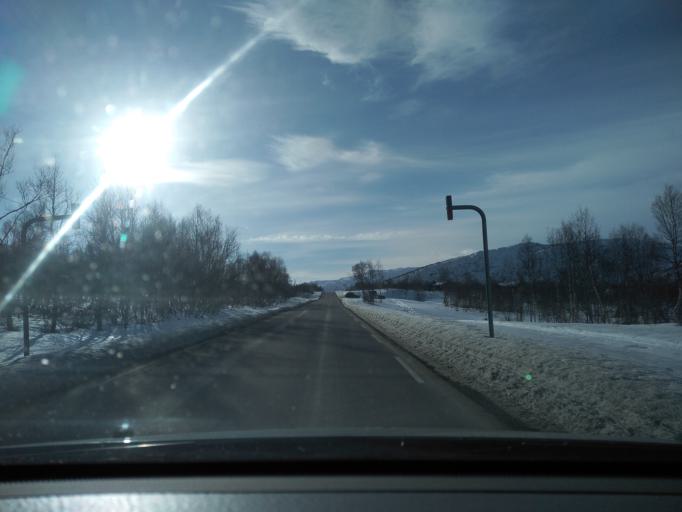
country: NO
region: Aust-Agder
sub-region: Bykle
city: Hovden
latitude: 59.6488
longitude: 7.4710
